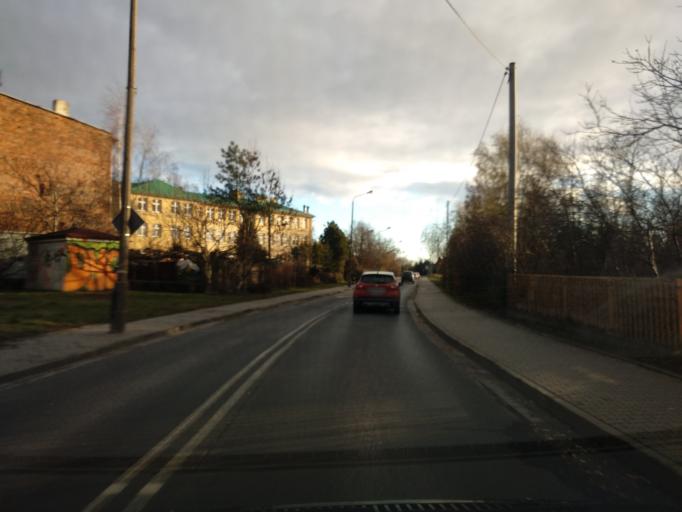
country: PL
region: Lower Silesian Voivodeship
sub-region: Powiat wroclawski
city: Zerniki Wroclawskie
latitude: 51.0562
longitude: 17.0259
